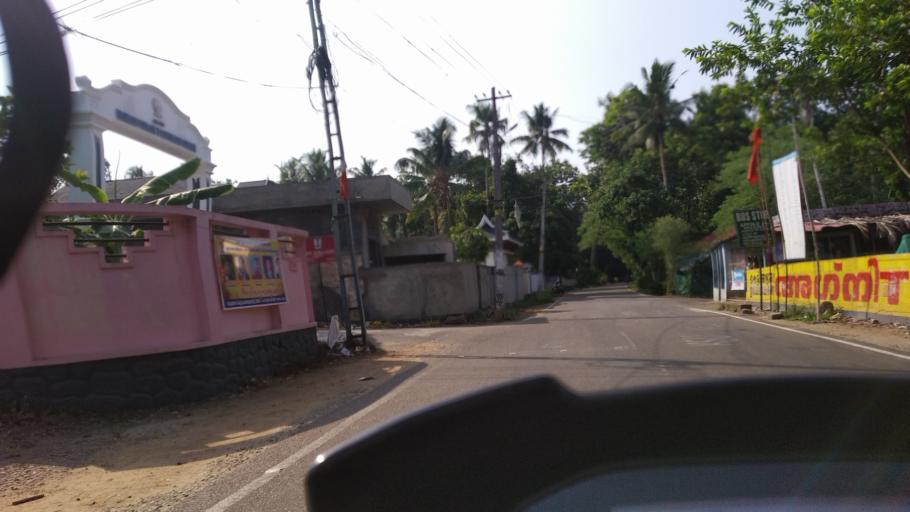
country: IN
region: Kerala
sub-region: Ernakulam
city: Piravam
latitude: 9.8631
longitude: 76.5145
